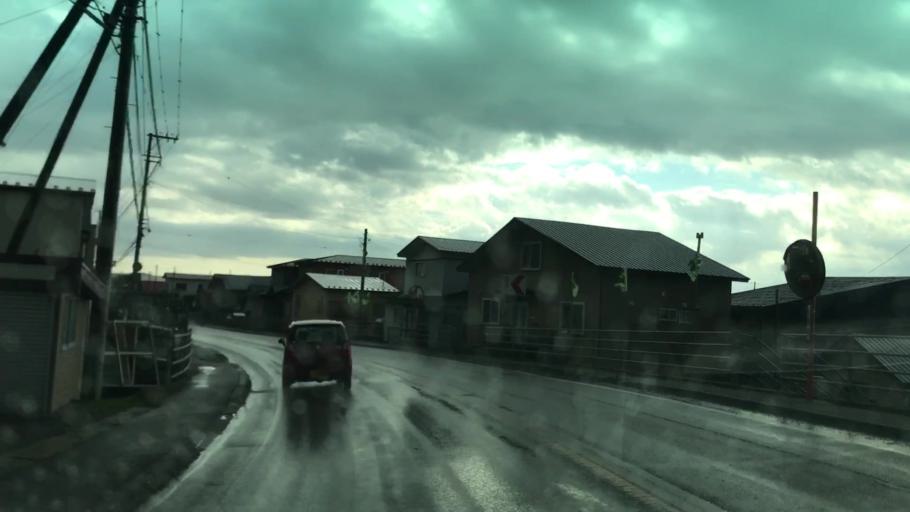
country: JP
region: Hokkaido
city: Shizunai-furukawacho
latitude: 42.1788
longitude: 142.7316
